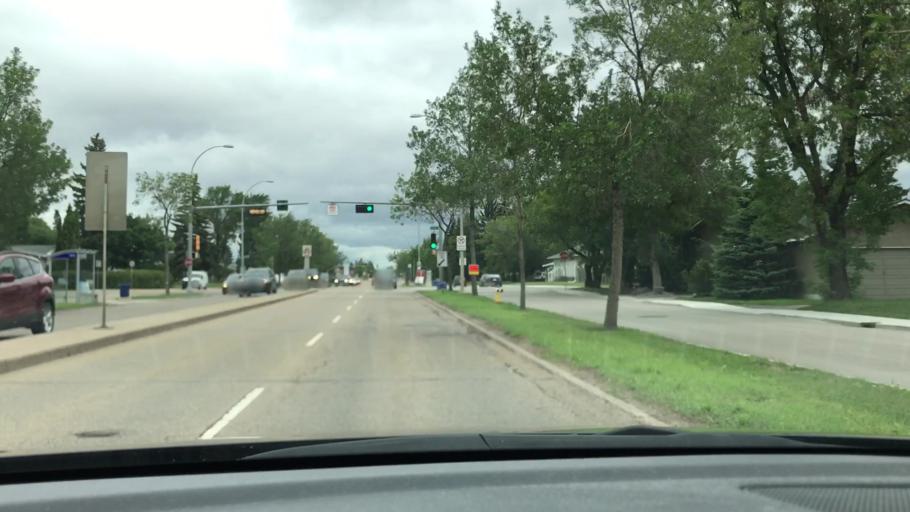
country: CA
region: Alberta
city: Edmonton
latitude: 53.5162
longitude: -113.5779
